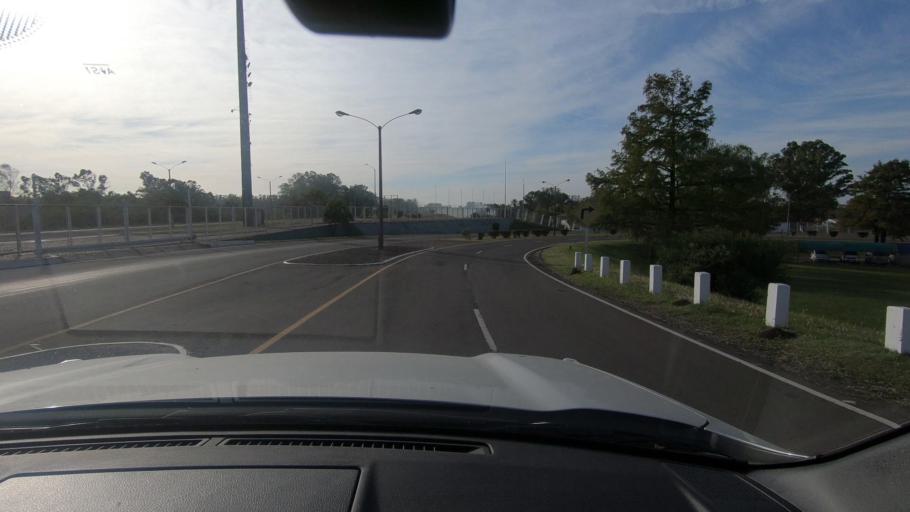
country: AR
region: Entre Rios
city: Colon
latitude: -32.2461
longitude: -58.1479
